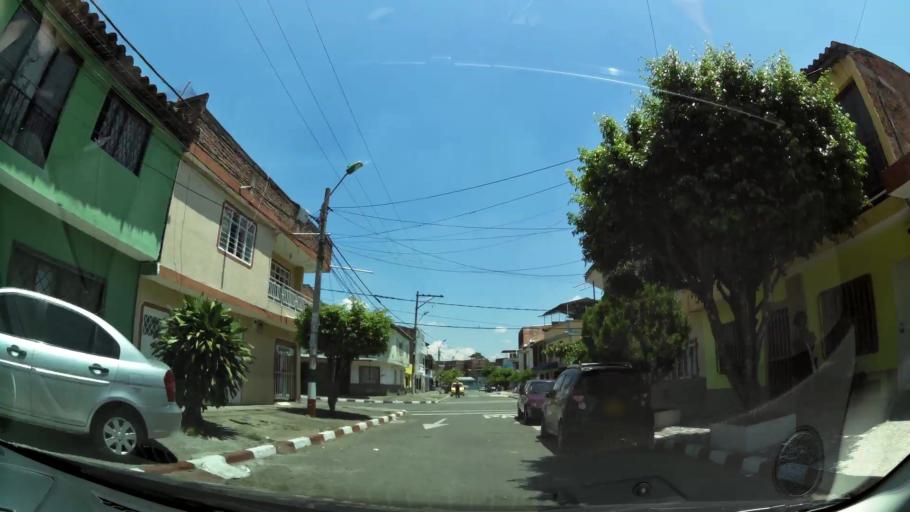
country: CO
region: Valle del Cauca
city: Cali
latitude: 3.4299
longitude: -76.5054
